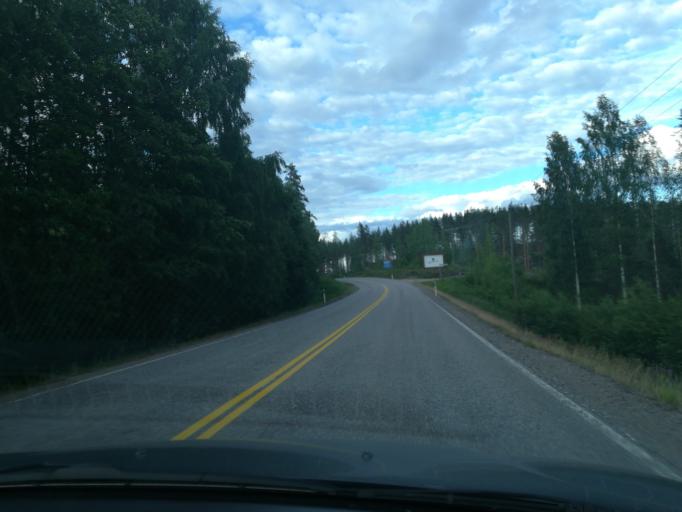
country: FI
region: Southern Savonia
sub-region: Mikkeli
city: Puumala
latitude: 61.5701
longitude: 28.1301
